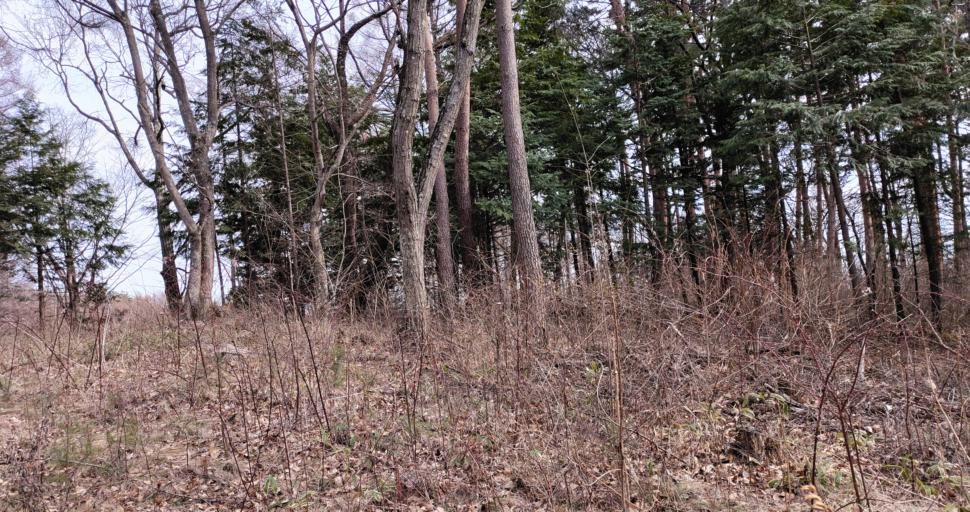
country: JP
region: Nagano
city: Komoro
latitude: 36.3705
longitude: 138.4485
